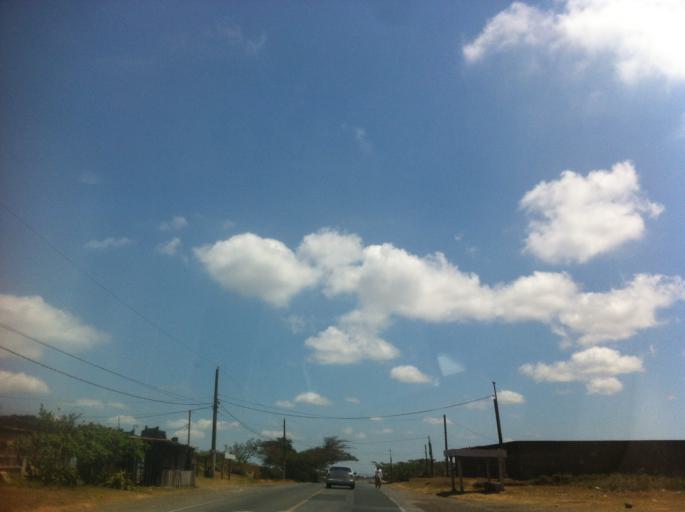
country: NI
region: Managua
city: El Crucero
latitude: 11.9629
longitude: -86.3056
